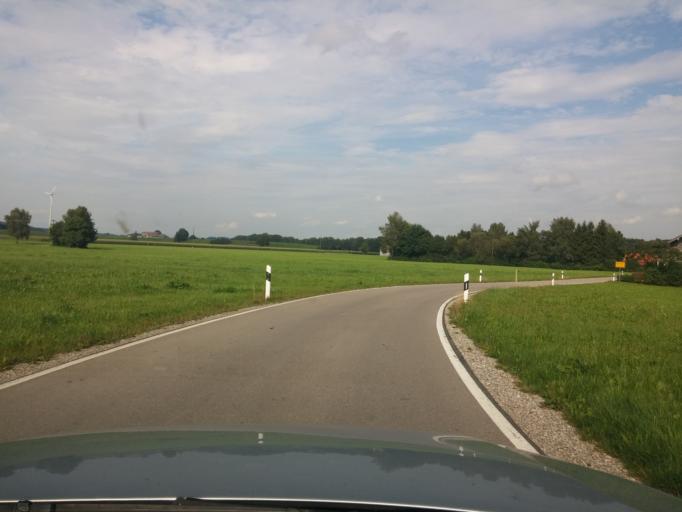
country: DE
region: Bavaria
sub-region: Swabia
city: Legau
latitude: 47.8422
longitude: 10.1592
